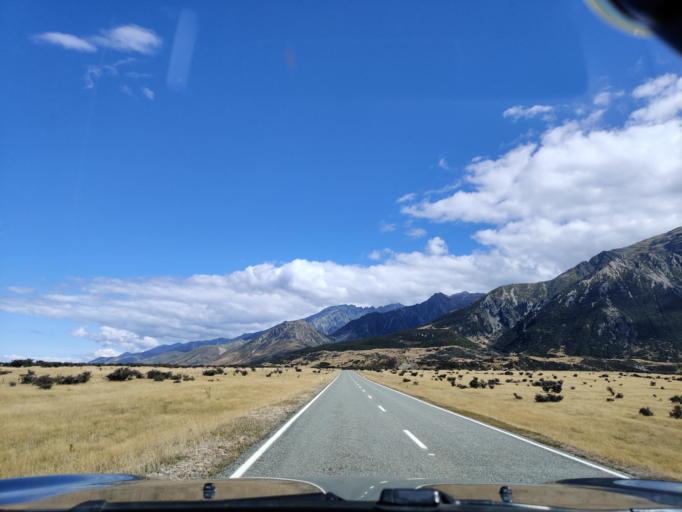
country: NZ
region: Canterbury
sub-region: Timaru District
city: Pleasant Point
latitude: -43.7948
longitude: 170.1165
